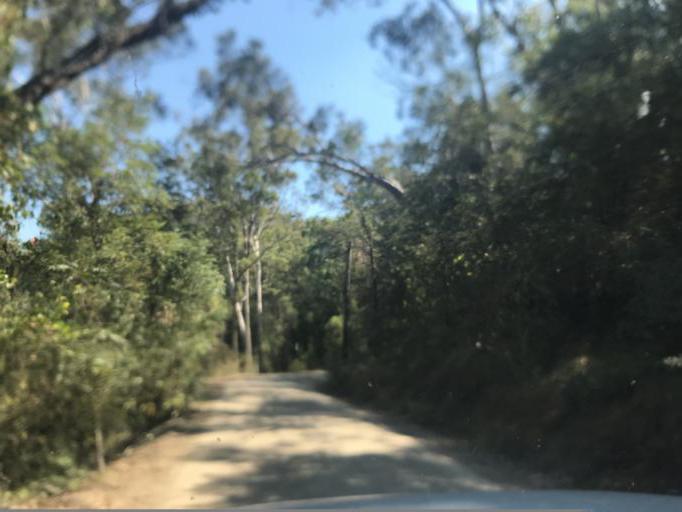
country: AU
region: New South Wales
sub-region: Hawkesbury
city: Pitt Town
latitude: -33.4184
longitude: 150.9030
